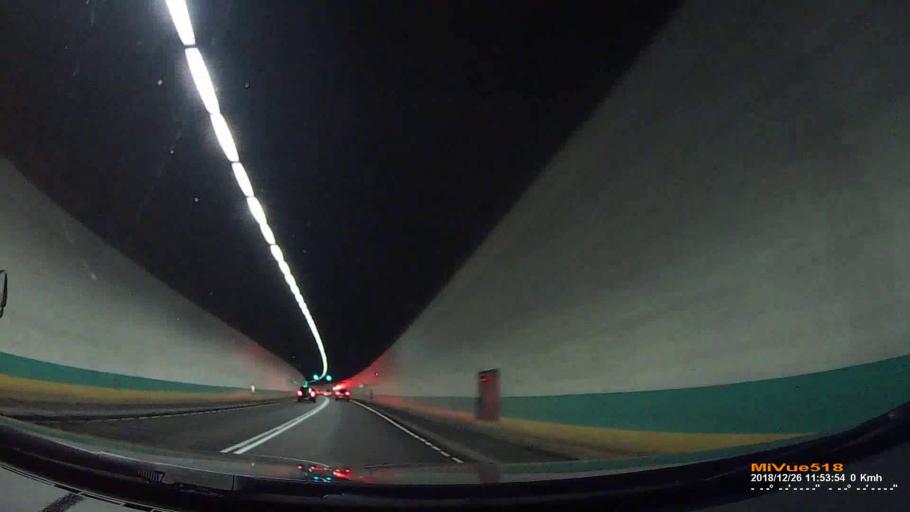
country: TW
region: Taiwan
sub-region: Keelung
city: Keelung
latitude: 24.9546
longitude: 121.6962
